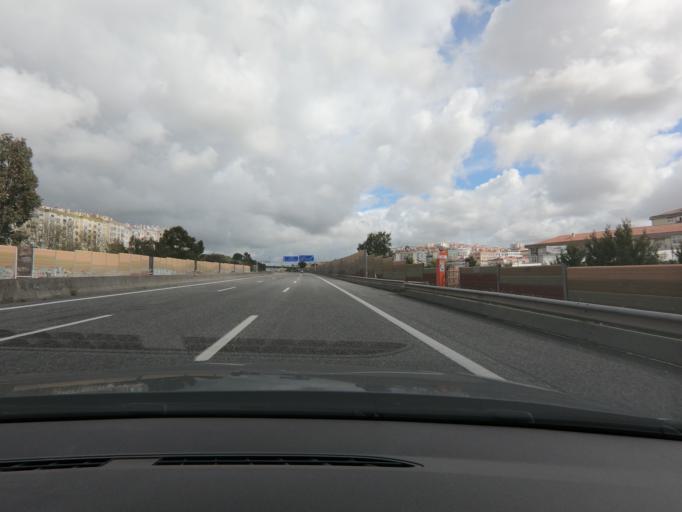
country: PT
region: Lisbon
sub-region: Sintra
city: Queluz
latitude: 38.7570
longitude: -9.2709
